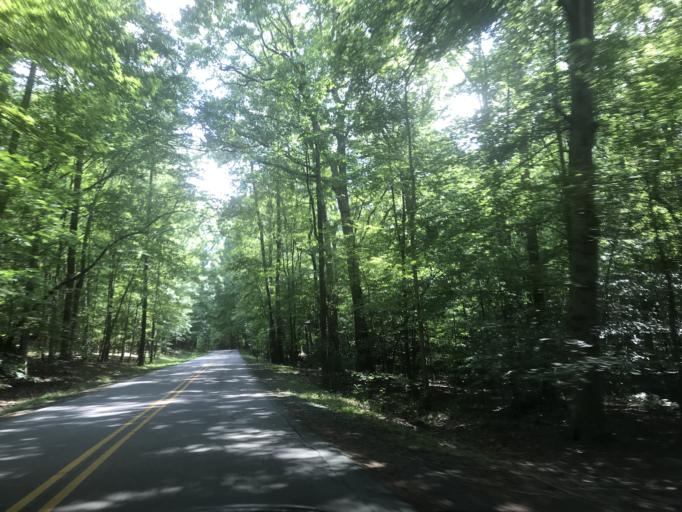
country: US
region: North Carolina
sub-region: Wake County
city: Morrisville
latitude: 35.8838
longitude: -78.7580
